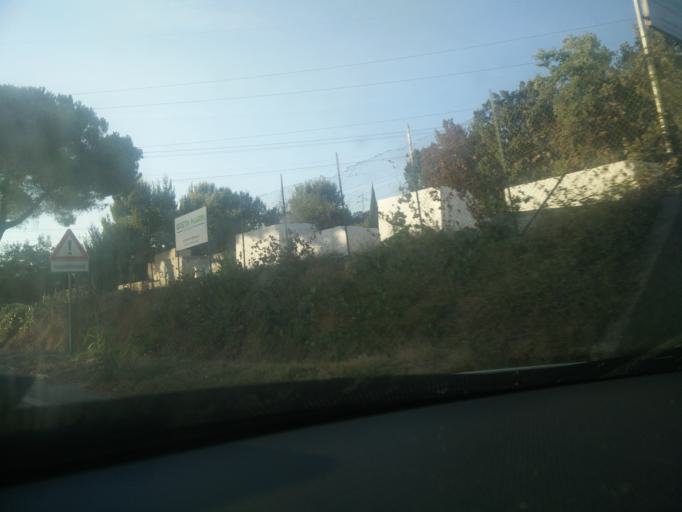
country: IT
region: Tuscany
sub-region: Provincia di Massa-Carrara
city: Carrara
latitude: 44.0459
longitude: 10.0820
